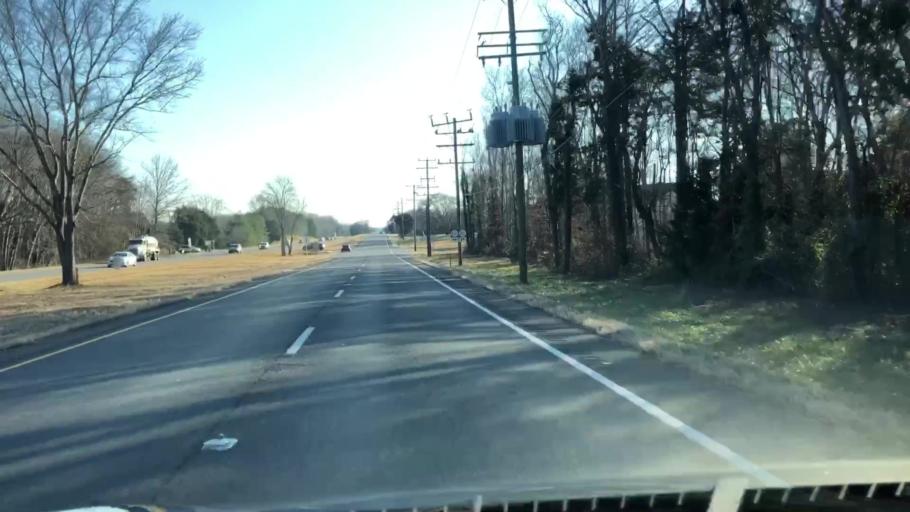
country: US
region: Virginia
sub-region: Fauquier County
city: Bealeton
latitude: 38.5828
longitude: -77.8024
